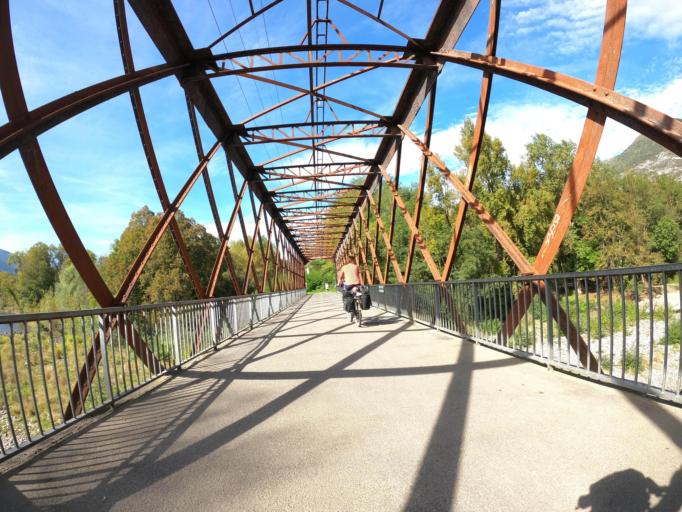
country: FR
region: Midi-Pyrenees
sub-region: Departement des Hautes-Pyrenees
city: Argeles-Gazost
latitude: 43.0222
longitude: -0.0826
